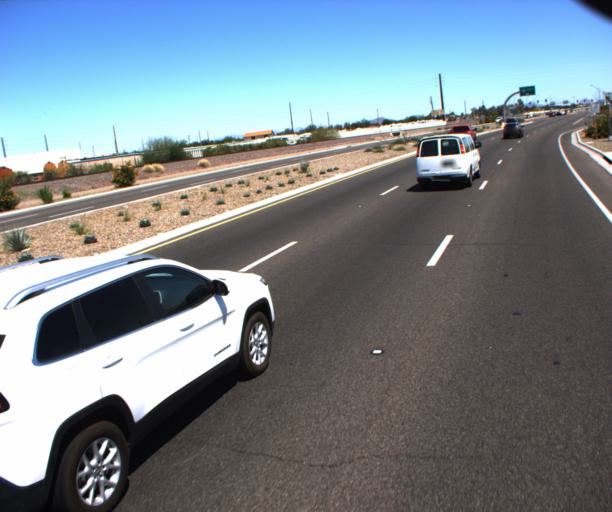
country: US
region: Arizona
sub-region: Maricopa County
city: Sun City
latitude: 33.5934
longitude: -112.2586
